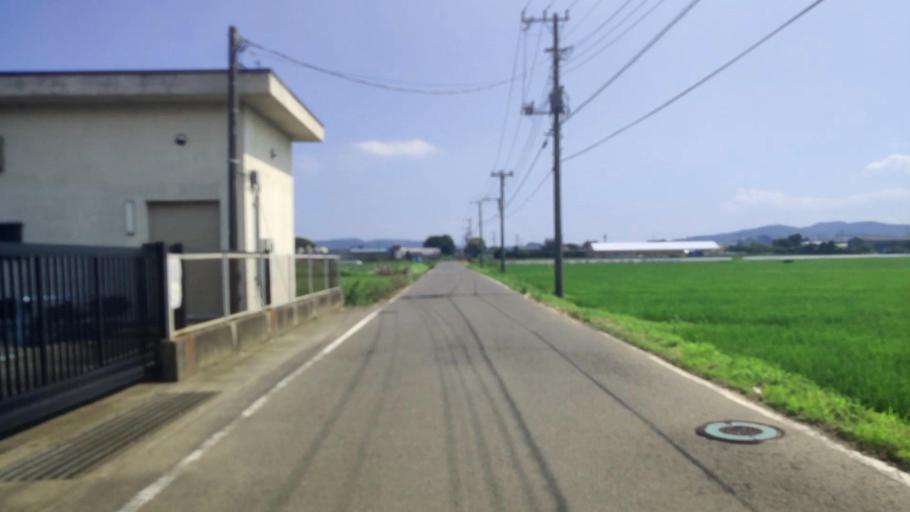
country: JP
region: Kanagawa
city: Isehara
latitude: 35.3699
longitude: 139.3073
